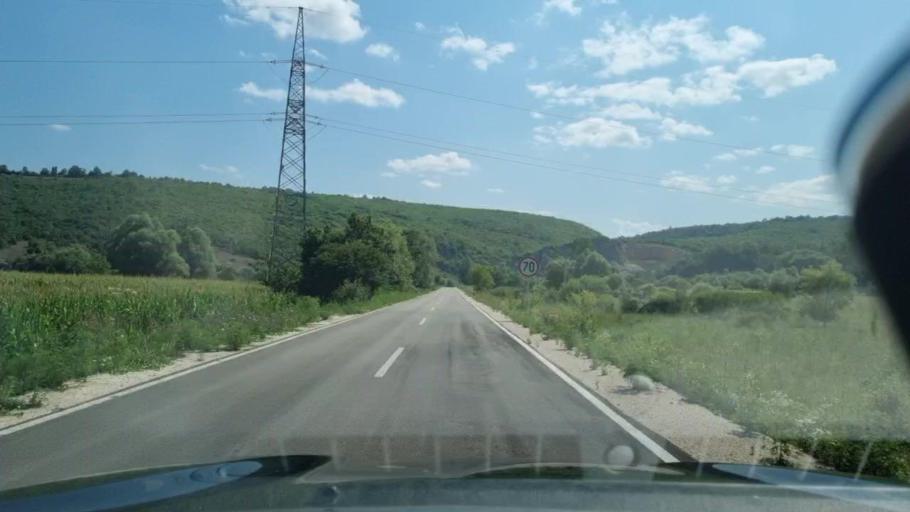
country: BA
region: Federation of Bosnia and Herzegovina
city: Kljuc
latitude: 44.5547
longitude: 16.7969
